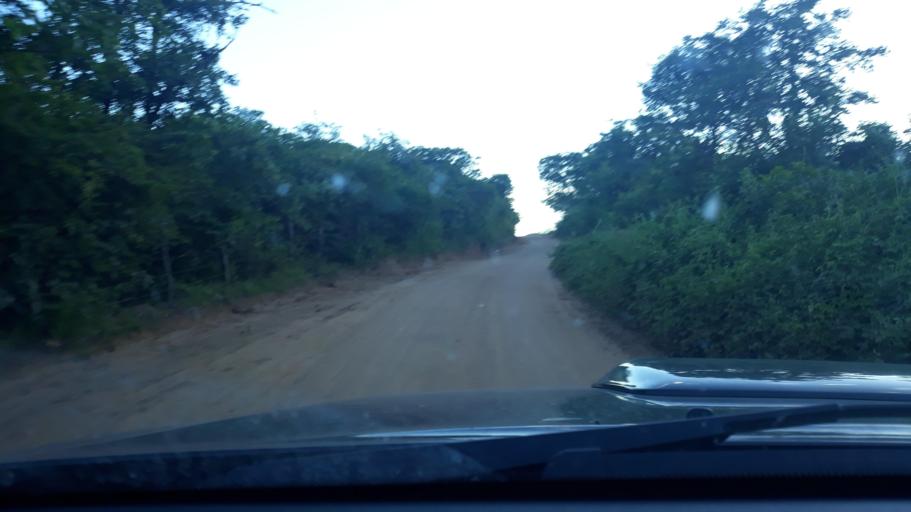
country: BR
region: Bahia
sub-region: Riacho De Santana
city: Riacho de Santana
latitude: -13.8165
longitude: -42.7233
